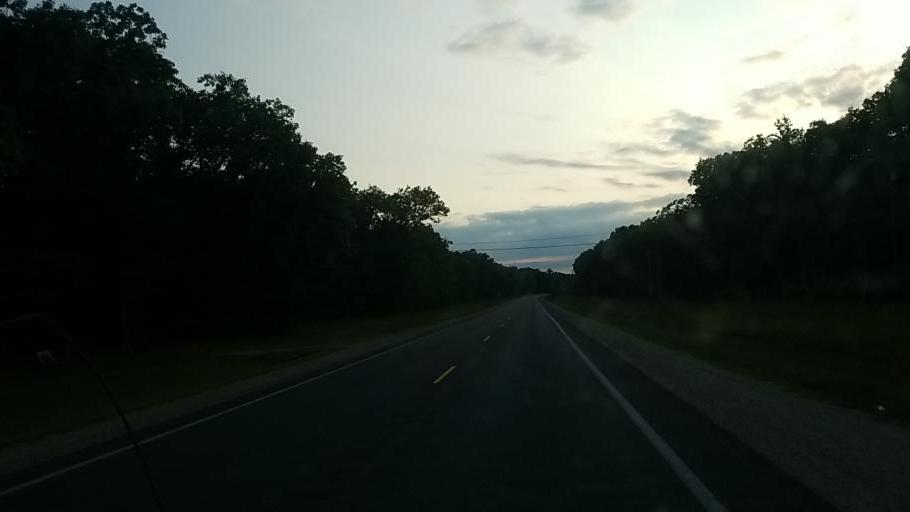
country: US
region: Michigan
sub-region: Newaygo County
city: Newaygo
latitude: 43.4047
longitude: -85.7288
